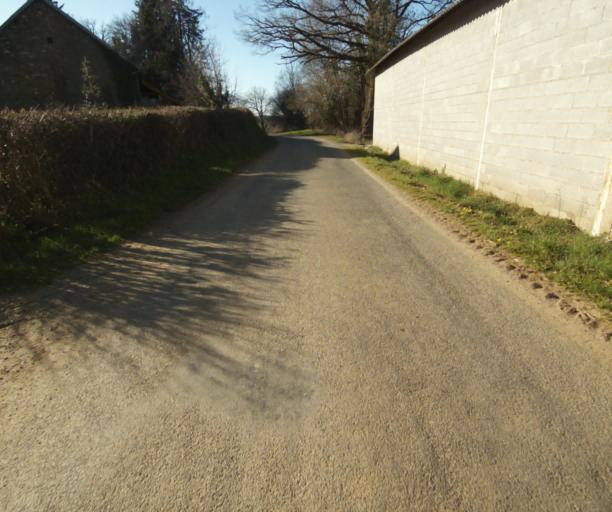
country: FR
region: Limousin
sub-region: Departement de la Correze
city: Seilhac
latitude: 45.3794
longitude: 1.7129
